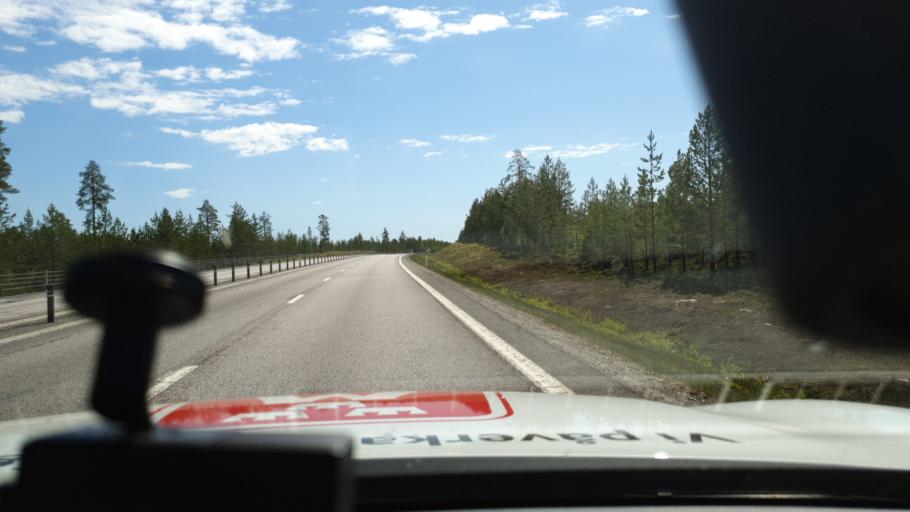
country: SE
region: Norrbotten
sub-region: Pitea Kommun
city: Pitea
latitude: 65.2221
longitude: 21.5161
